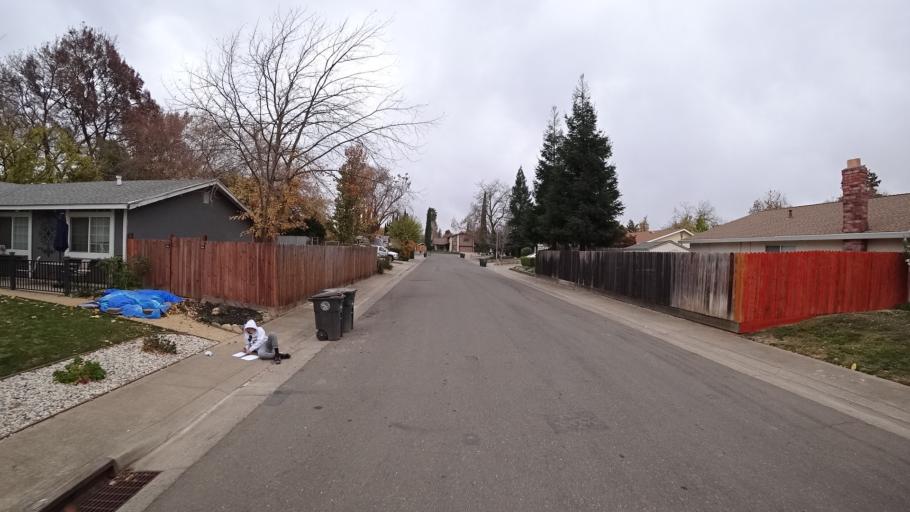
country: US
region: California
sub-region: Sacramento County
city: Citrus Heights
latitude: 38.6947
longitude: -121.3030
